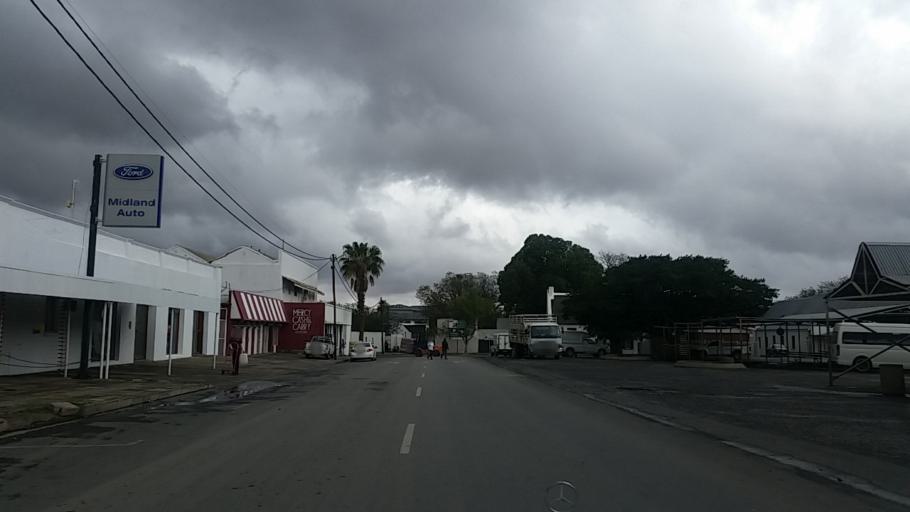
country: ZA
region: Eastern Cape
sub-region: Cacadu District Municipality
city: Graaff-Reinet
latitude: -32.2493
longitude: 24.5382
